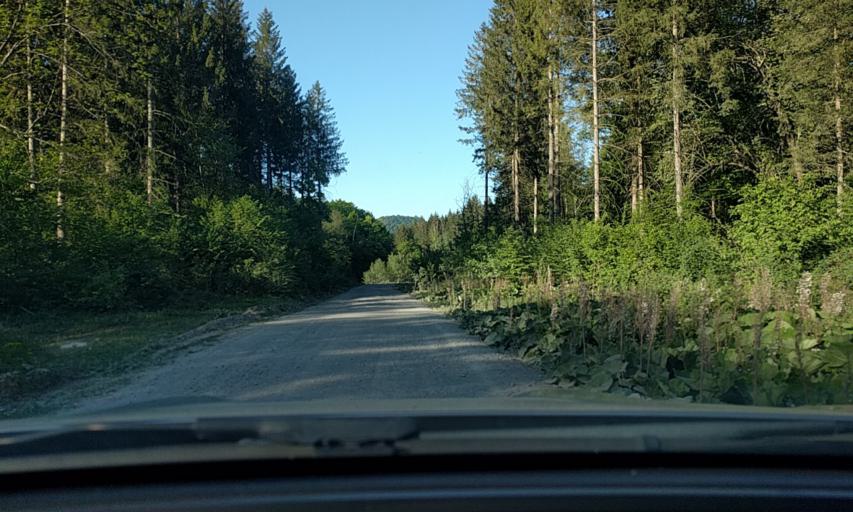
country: RO
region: Bacau
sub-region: Comuna Oituz
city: Ferestrau-Oituz
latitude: 46.1651
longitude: 26.5675
